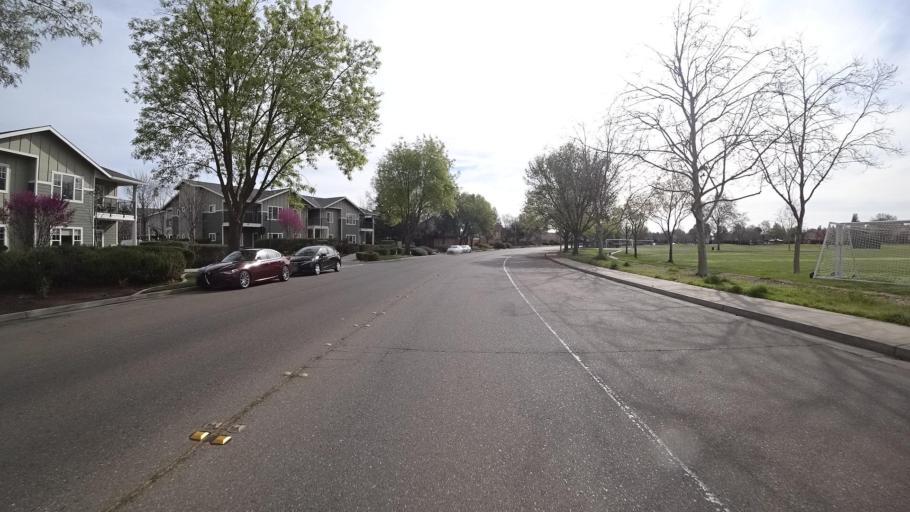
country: US
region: California
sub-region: Yolo County
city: Davis
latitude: 38.5709
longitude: -121.7281
